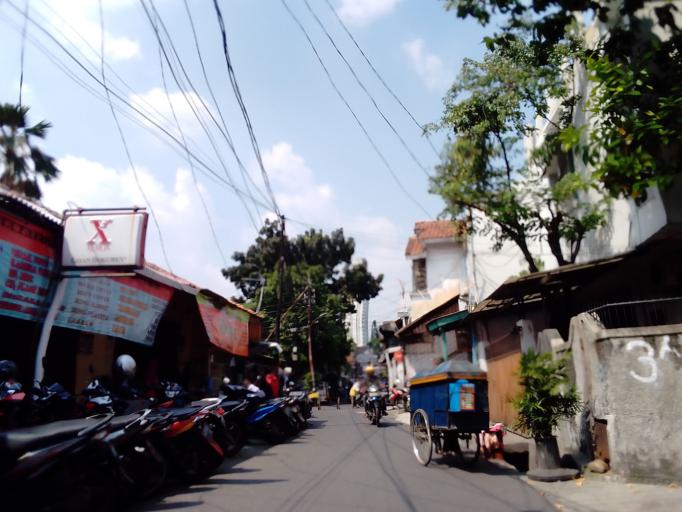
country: ID
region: Jakarta Raya
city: Jakarta
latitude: -6.2586
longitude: 106.8004
